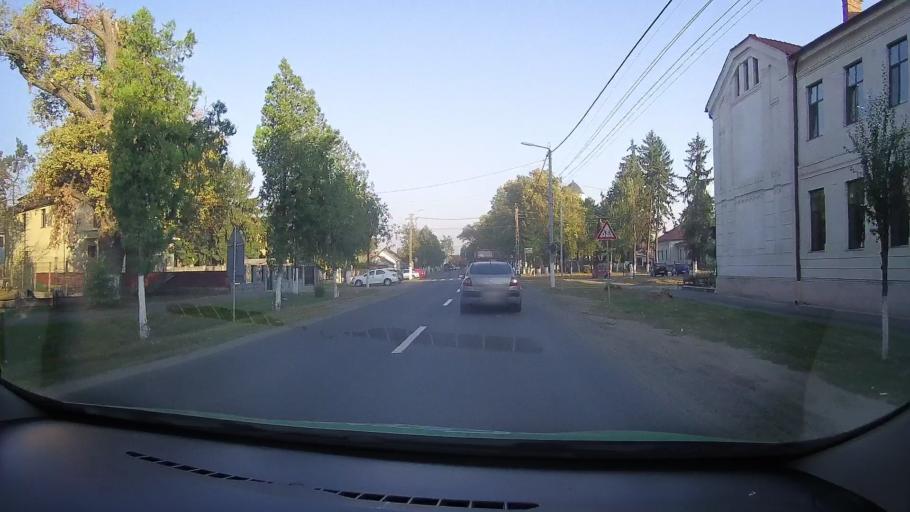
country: RO
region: Arad
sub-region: Comuna Curtici
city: Curtici
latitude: 46.3402
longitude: 21.3083
